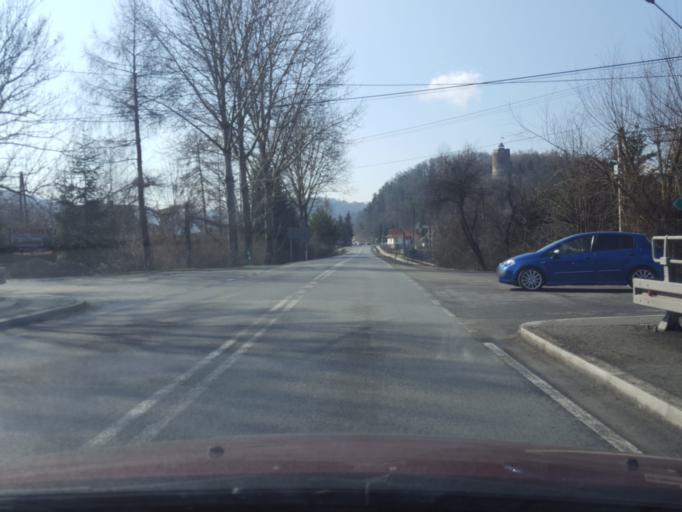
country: PL
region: Lesser Poland Voivodeship
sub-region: Powiat brzeski
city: Czchow
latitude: 49.8371
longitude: 20.6804
